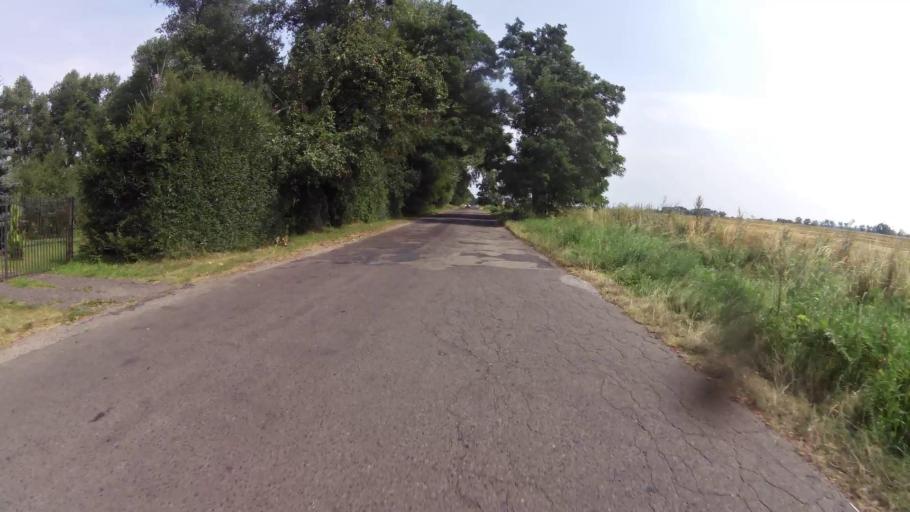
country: PL
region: West Pomeranian Voivodeship
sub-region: Powiat pyrzycki
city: Lipiany
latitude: 52.9722
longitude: 14.9762
